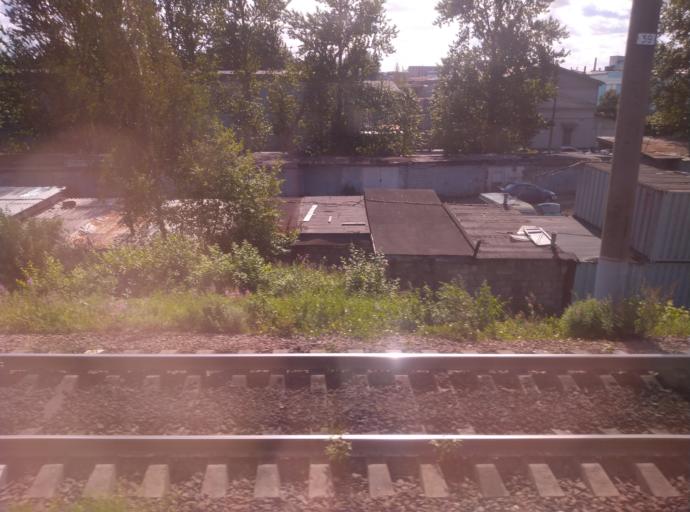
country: RU
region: St.-Petersburg
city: Centralniy
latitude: 59.9099
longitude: 30.3906
